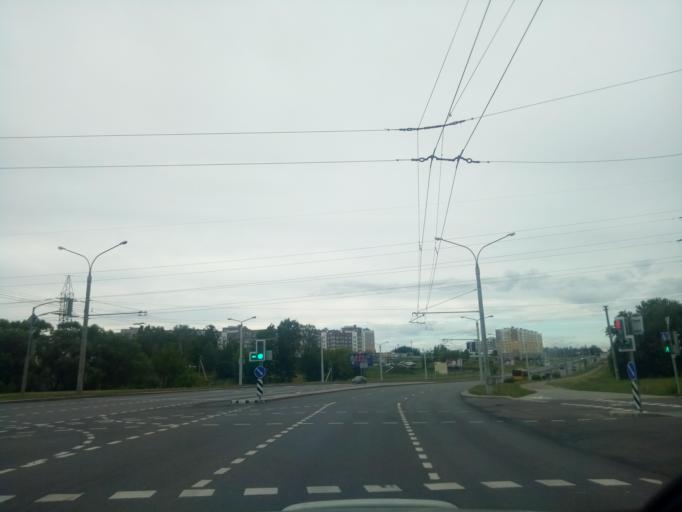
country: BY
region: Minsk
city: Novoye Medvezhino
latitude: 53.8744
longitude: 27.4770
